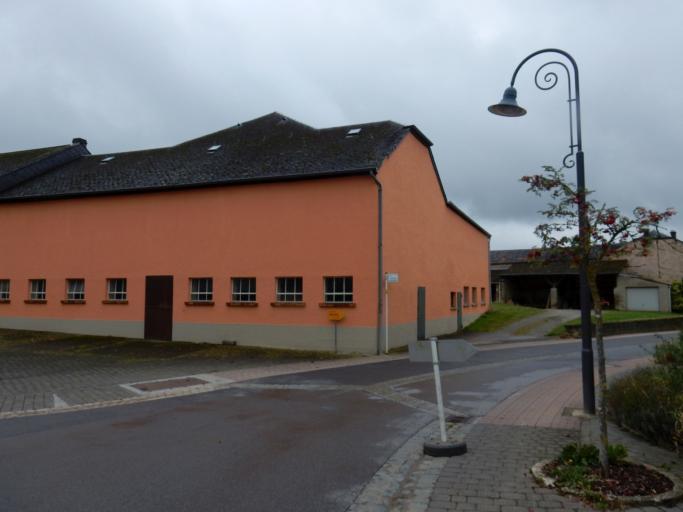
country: LU
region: Luxembourg
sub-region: Canton de Luxembourg
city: Olm
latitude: 49.6756
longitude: 6.0081
